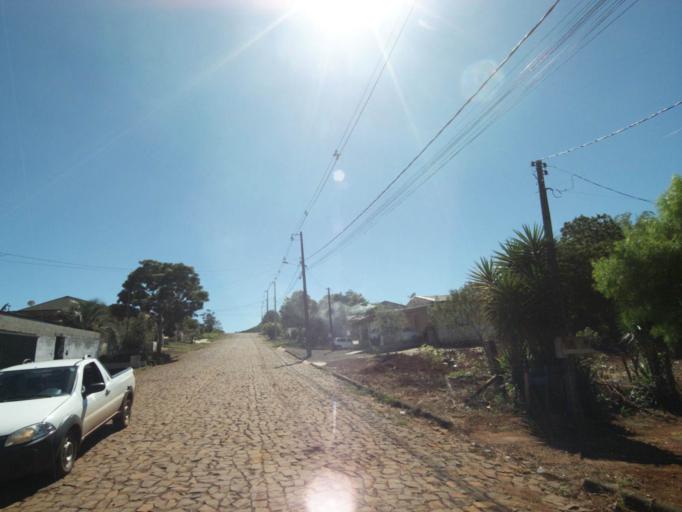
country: BR
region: Santa Catarina
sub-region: Sao Lourenco Do Oeste
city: Sao Lourenco dOeste
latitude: -26.2709
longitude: -52.7822
